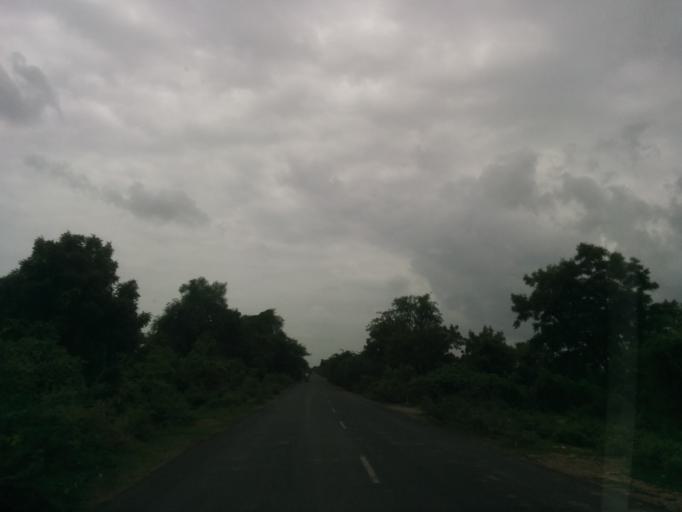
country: IN
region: Gujarat
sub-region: Ahmadabad
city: Sanand
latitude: 23.0725
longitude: 72.3959
